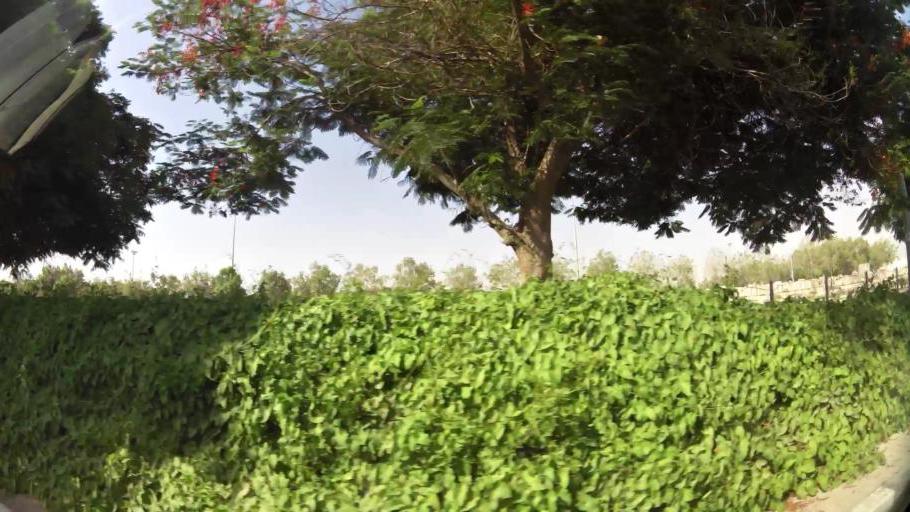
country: AE
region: Ash Shariqah
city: Sharjah
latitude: 25.2822
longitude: 55.3768
